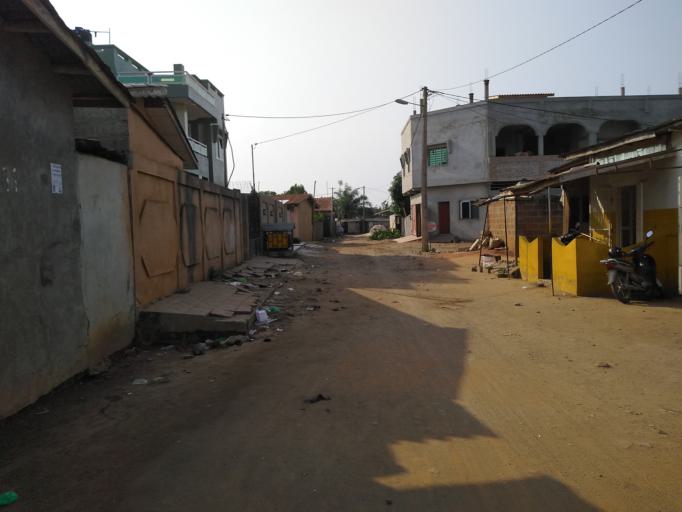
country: BJ
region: Atlantique
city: Abomey-Calavi
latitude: 6.4108
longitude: 2.3399
